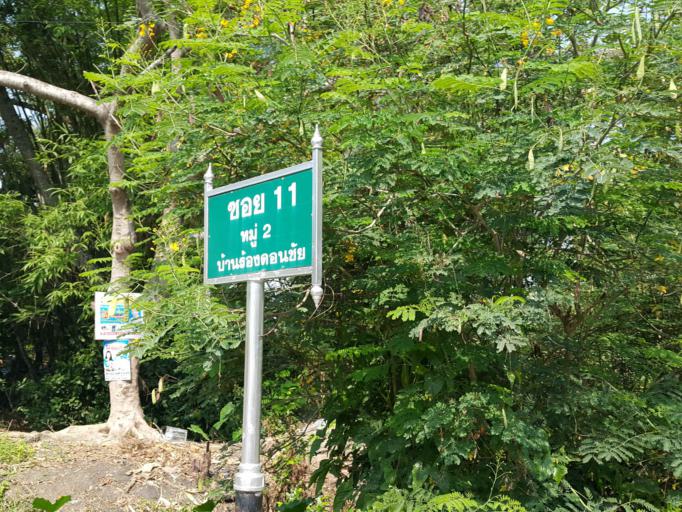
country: TH
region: Chiang Mai
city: Saraphi
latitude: 18.7443
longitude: 99.0524
